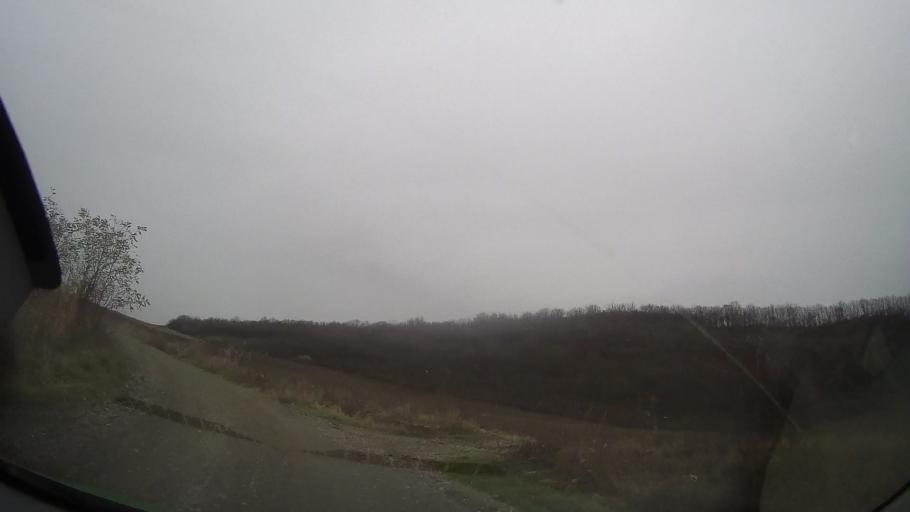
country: RO
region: Mures
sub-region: Comuna Ceausu de Campie
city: Ceausu de Campie
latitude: 46.6518
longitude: 24.4976
